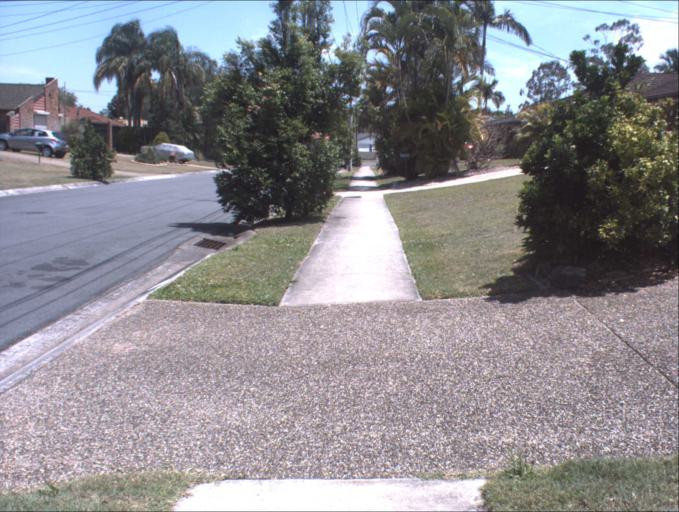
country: AU
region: Queensland
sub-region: Logan
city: Slacks Creek
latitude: -27.6352
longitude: 153.1437
